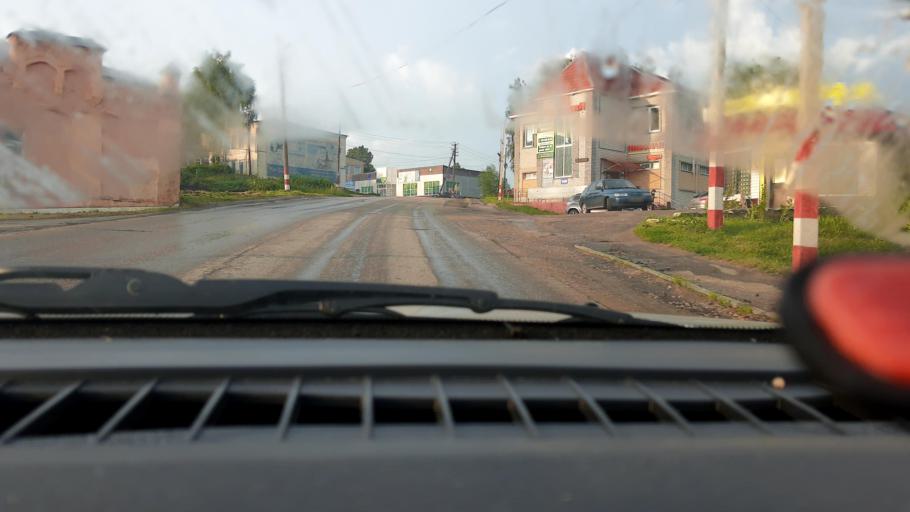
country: RU
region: Nizjnij Novgorod
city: Lukoyanov
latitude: 55.0314
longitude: 44.4939
